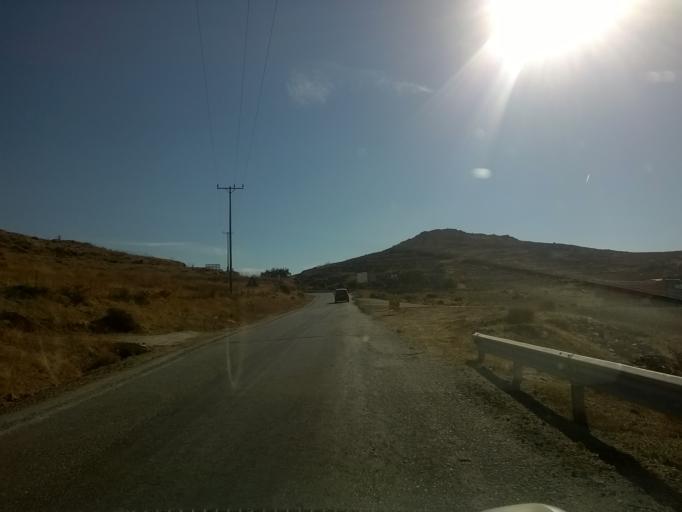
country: GR
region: South Aegean
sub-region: Nomos Kykladon
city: Naxos
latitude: 37.1196
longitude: 25.4154
